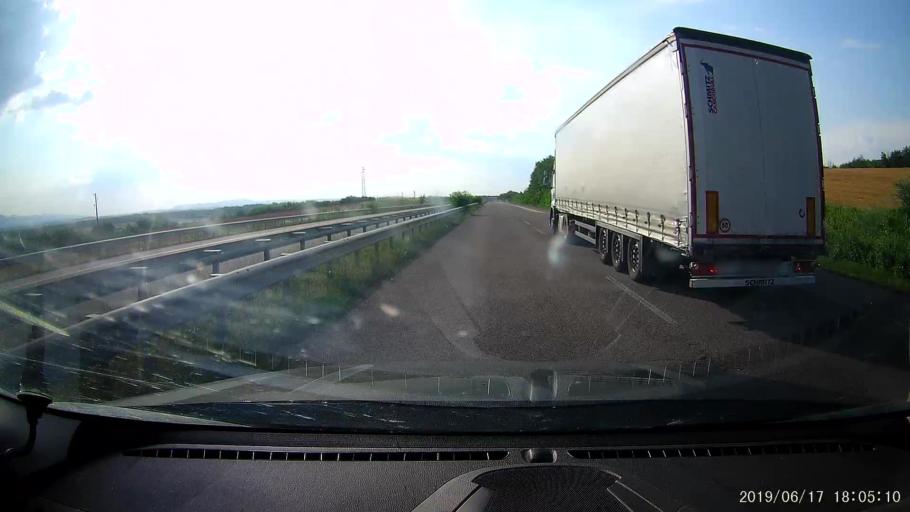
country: BG
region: Khaskovo
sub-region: Obshtina Svilengrad
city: Svilengrad
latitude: 41.7949
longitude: 26.1817
